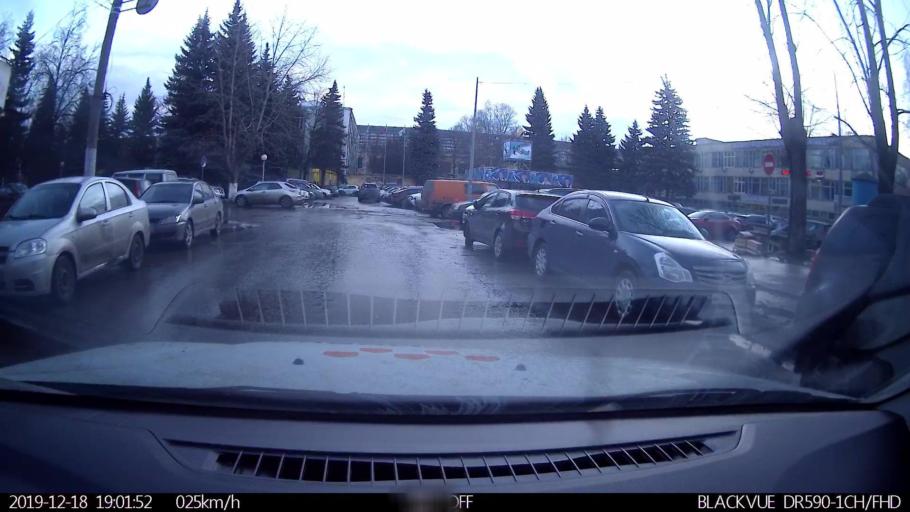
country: RU
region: Nizjnij Novgorod
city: Gorbatovka
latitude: 56.3284
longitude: 43.8571
